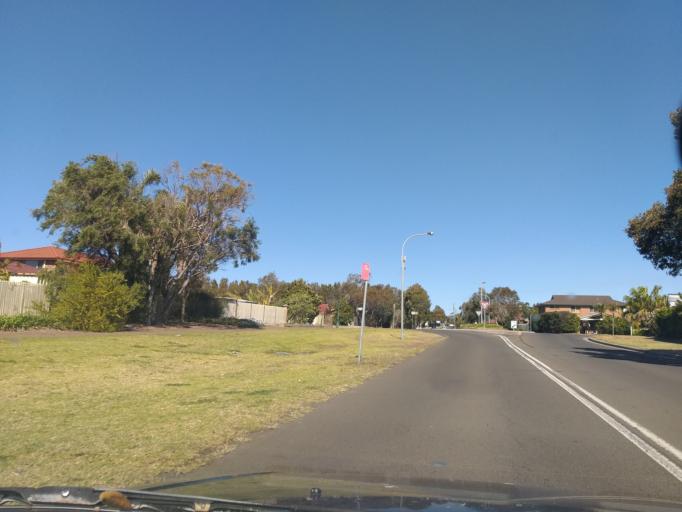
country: AU
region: New South Wales
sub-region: Wollongong
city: East Corrimal
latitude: -34.3594
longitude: 150.9127
